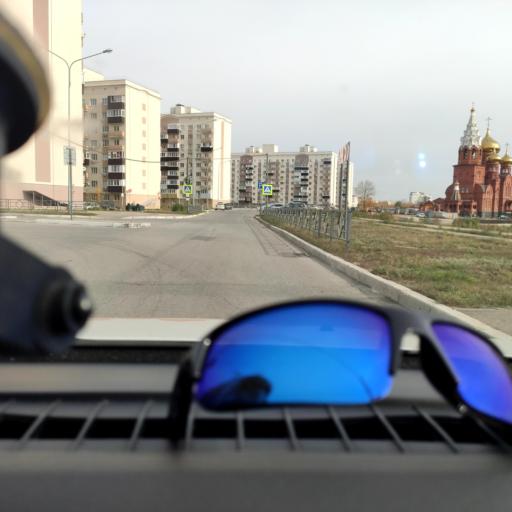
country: RU
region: Samara
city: Samara
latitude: 53.1101
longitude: 50.1445
